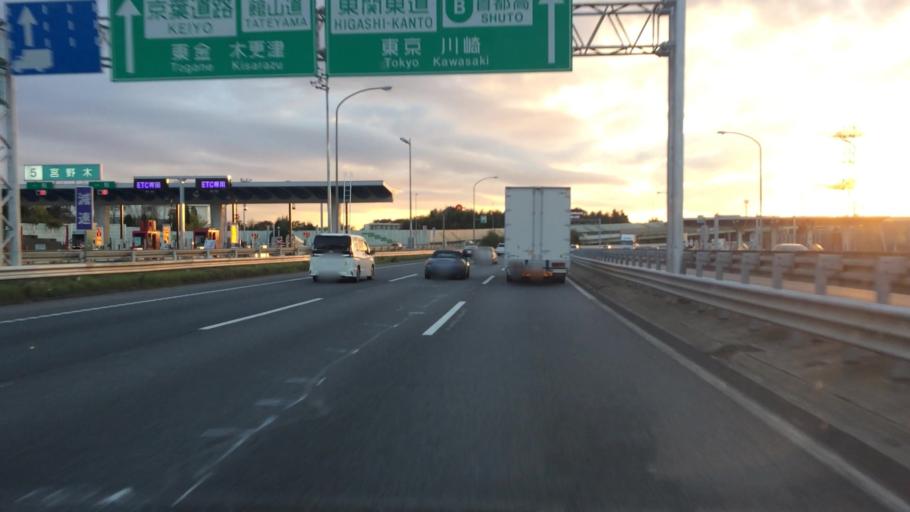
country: JP
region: Chiba
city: Yotsukaido
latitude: 35.6670
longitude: 140.1120
